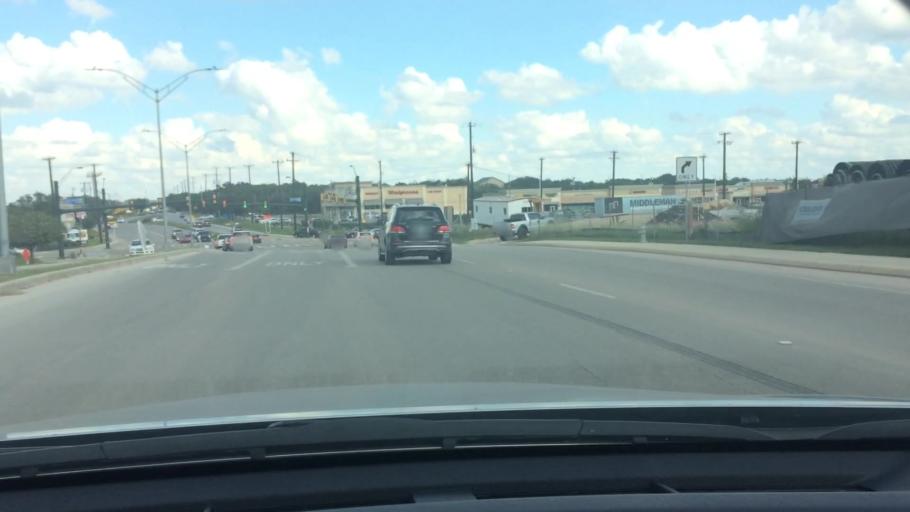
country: US
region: Texas
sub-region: Bexar County
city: Hollywood Park
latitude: 29.6474
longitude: -98.4268
